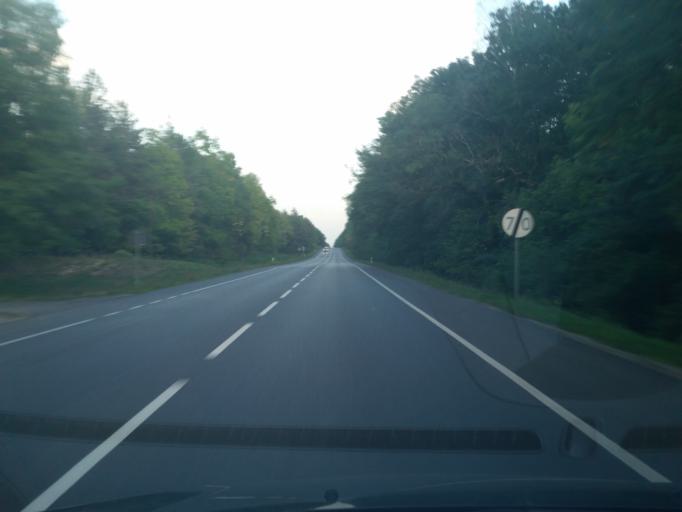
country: PL
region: Masovian Voivodeship
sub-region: Powiat warszawski zachodni
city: Kielpin
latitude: 52.3922
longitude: 20.8710
